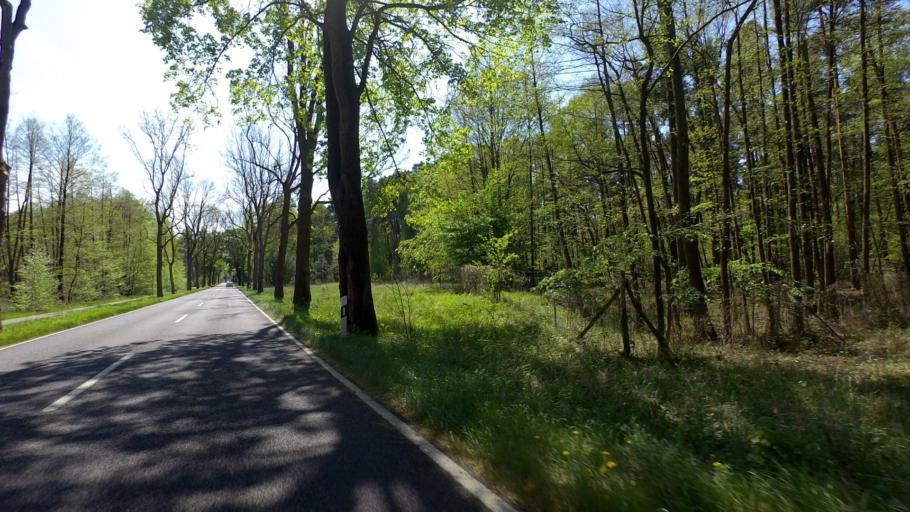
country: DE
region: Brandenburg
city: Halbe
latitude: 52.1397
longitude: 13.7490
